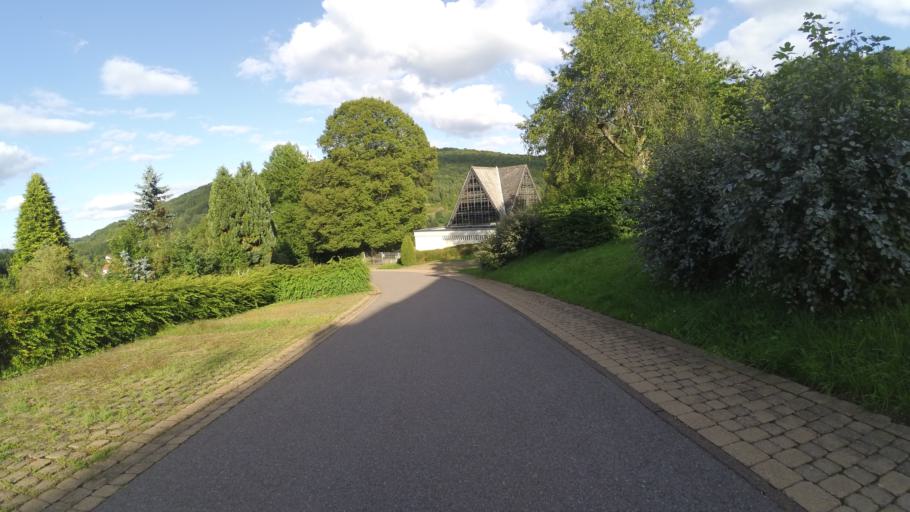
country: DE
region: Saarland
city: Nonnweiler
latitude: 49.5668
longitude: 6.9654
